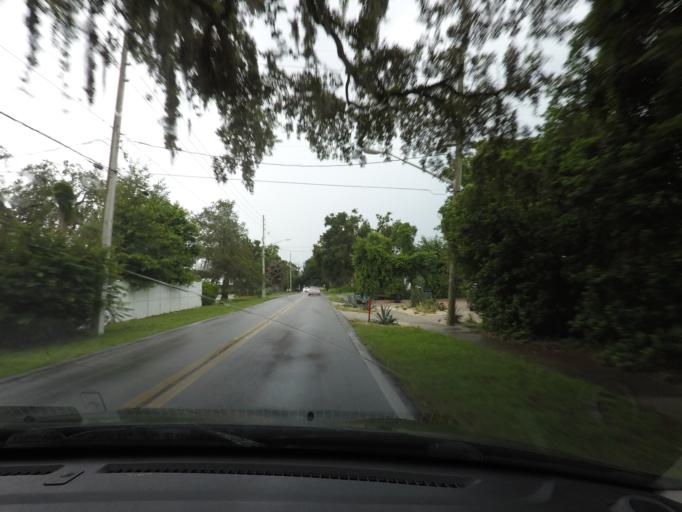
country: US
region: Florida
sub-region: Orange County
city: Edgewood
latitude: 28.5010
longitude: -81.3679
